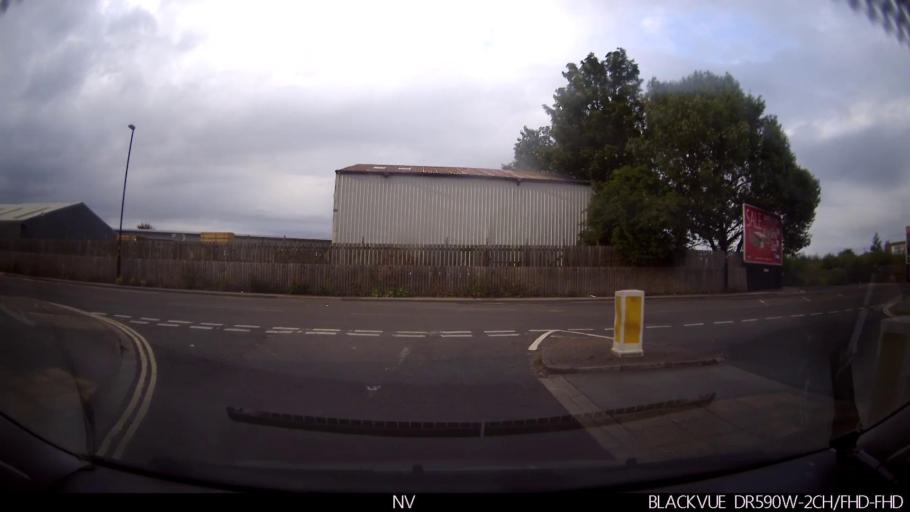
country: GB
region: England
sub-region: City of York
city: York
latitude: 53.9613
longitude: -1.1006
